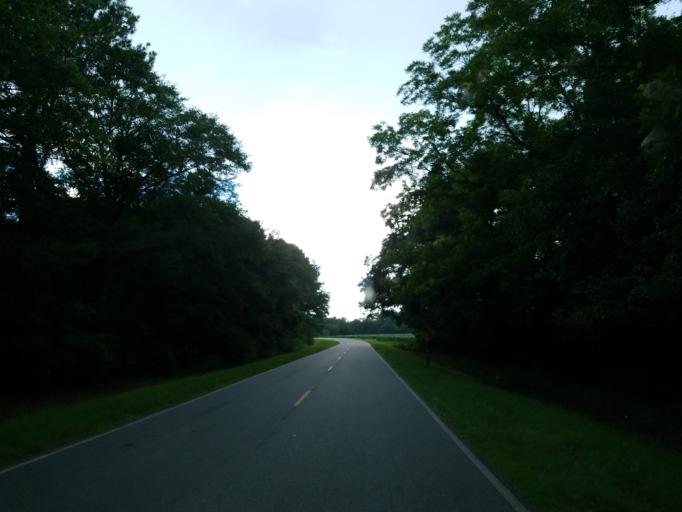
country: US
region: Georgia
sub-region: Tift County
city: Omega
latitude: 31.2575
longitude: -83.5297
